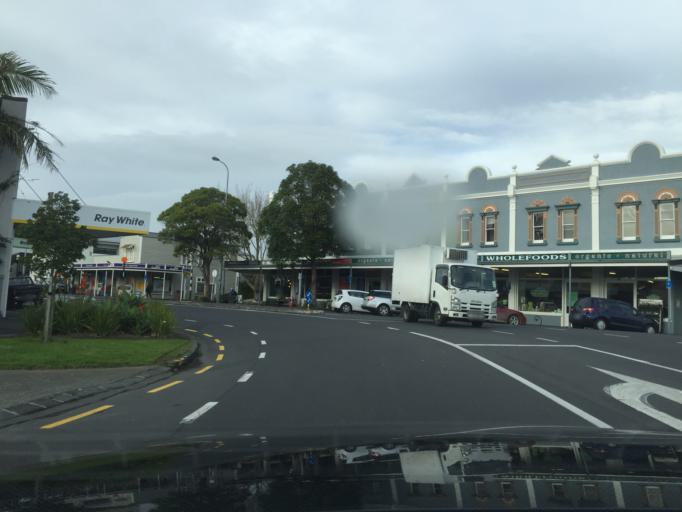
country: NZ
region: Auckland
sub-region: Auckland
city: Auckland
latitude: -36.8584
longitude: 174.7305
